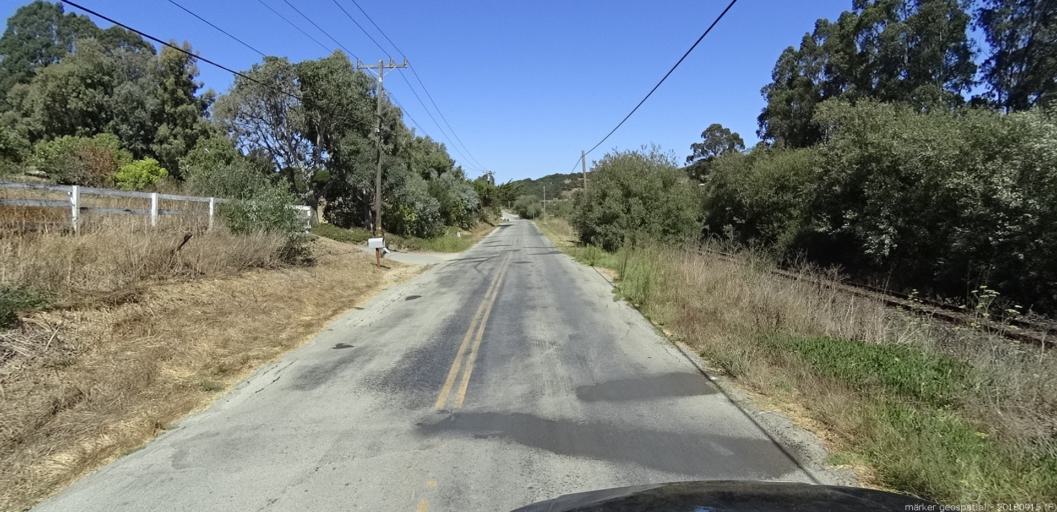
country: US
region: California
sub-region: Monterey County
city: Las Lomas
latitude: 36.8702
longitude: -121.7462
